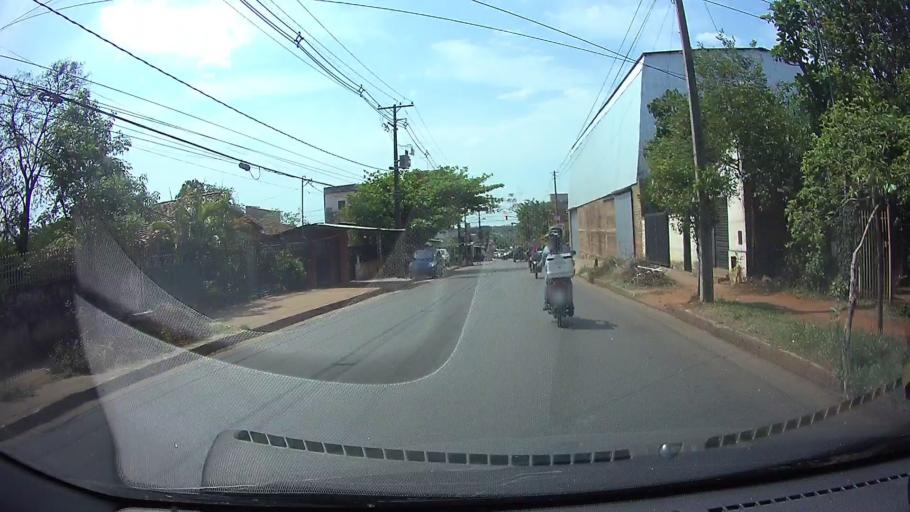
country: PY
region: Central
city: San Lorenzo
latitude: -25.3356
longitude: -57.4918
